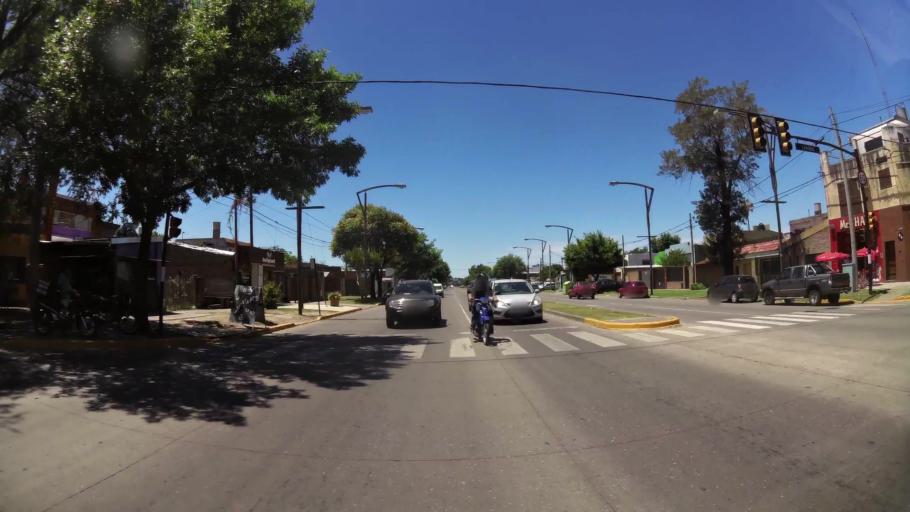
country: AR
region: Santa Fe
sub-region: Departamento de Rosario
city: Rosario
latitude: -32.9481
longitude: -60.6983
